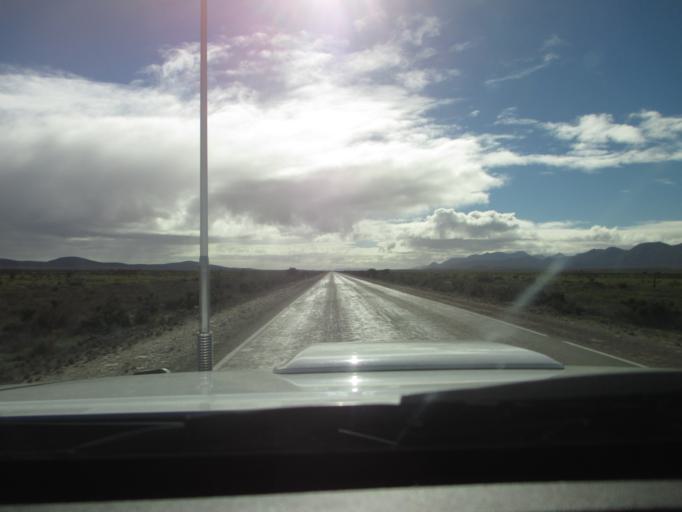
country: AU
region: South Australia
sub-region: Flinders Ranges
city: Quorn
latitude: -31.6915
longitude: 138.3611
